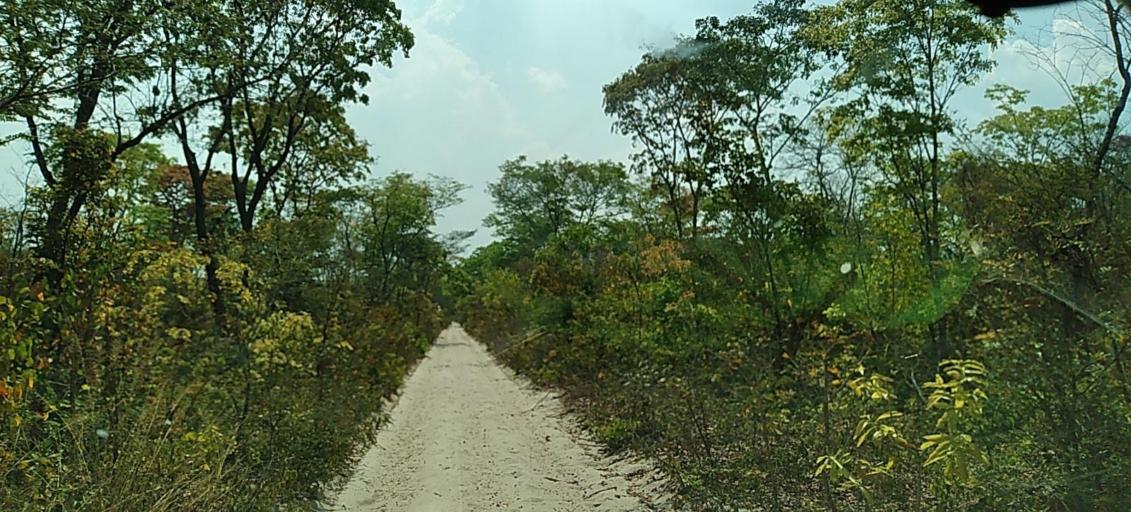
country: ZM
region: North-Western
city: Kabompo
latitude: -13.3961
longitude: 23.7992
